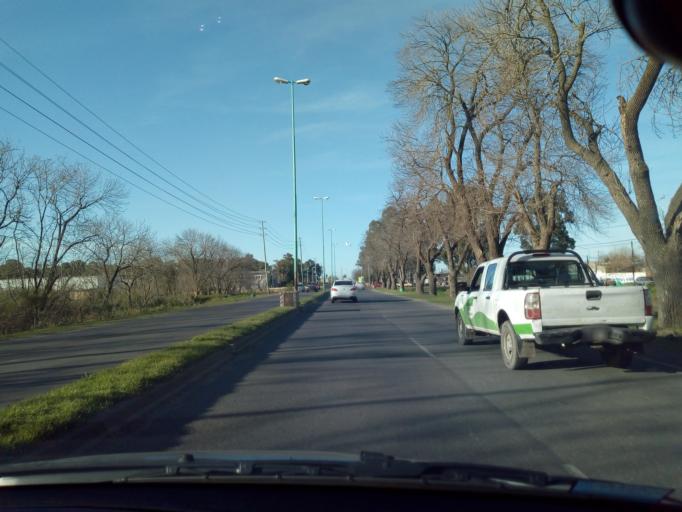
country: AR
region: Buenos Aires
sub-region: Partido de Ensenada
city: Ensenada
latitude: -34.8737
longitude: -57.9153
